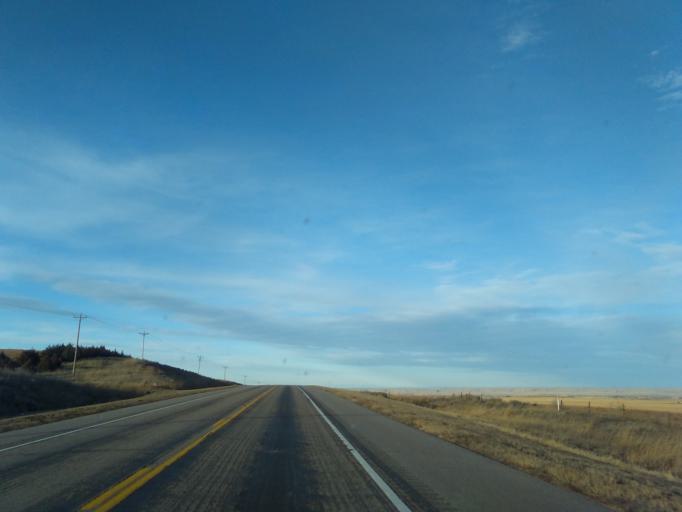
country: US
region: Nebraska
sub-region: Morrill County
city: Bridgeport
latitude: 41.5665
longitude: -102.9846
